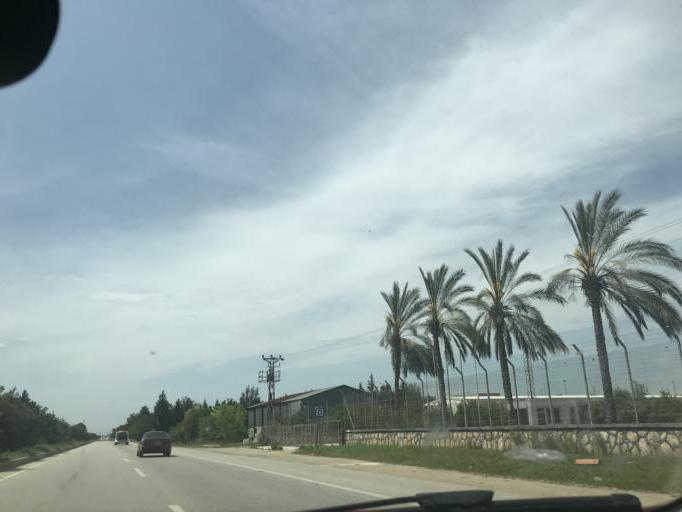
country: TR
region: Adana
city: Yakapinar
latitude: 36.9718
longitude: 35.5183
